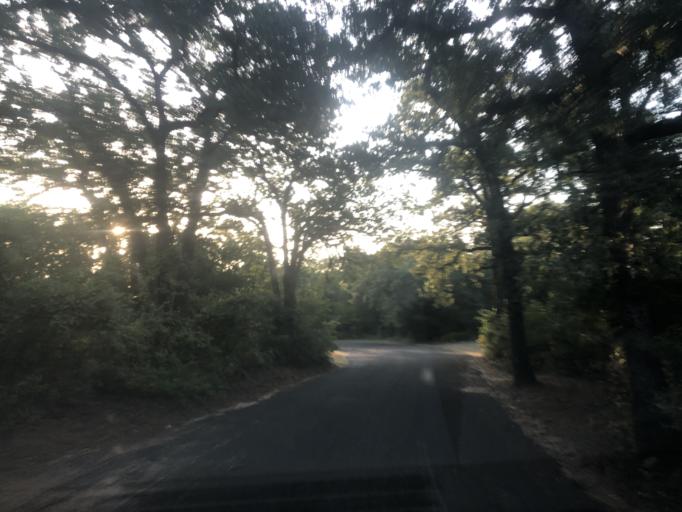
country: US
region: Texas
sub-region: Tarrant County
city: Lakeside
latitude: 32.7989
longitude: -97.4927
